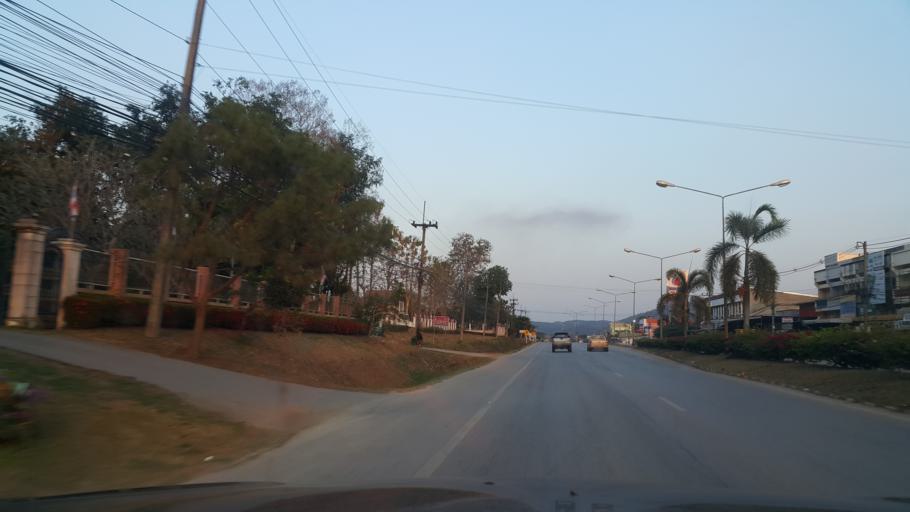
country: TH
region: Loei
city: Loei
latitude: 17.4938
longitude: 101.7091
